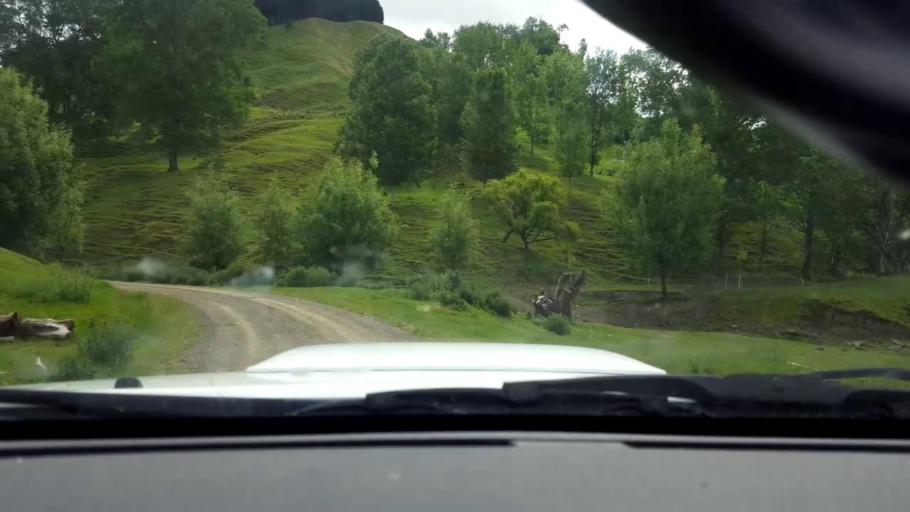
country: NZ
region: Gisborne
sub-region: Gisborne District
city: Gisborne
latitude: -38.4897
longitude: 177.6822
